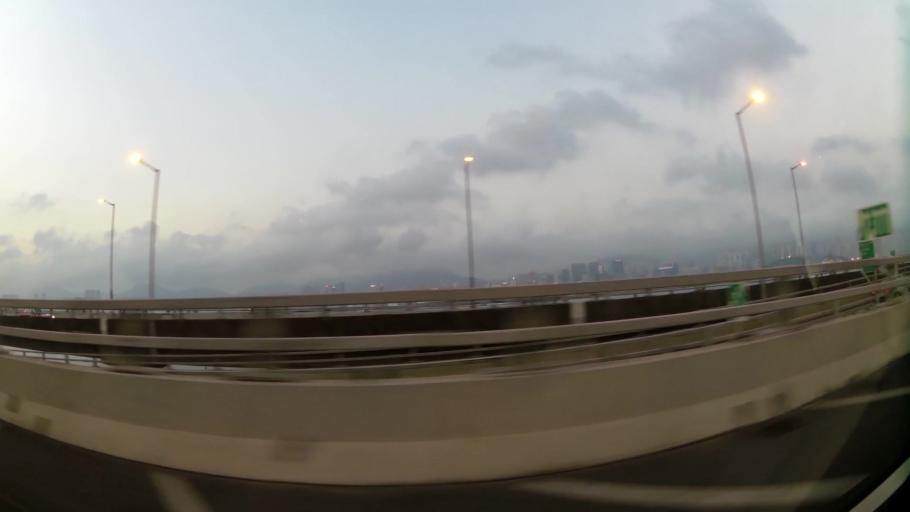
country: HK
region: Kowloon City
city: Kowloon
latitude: 22.2936
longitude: 114.2068
